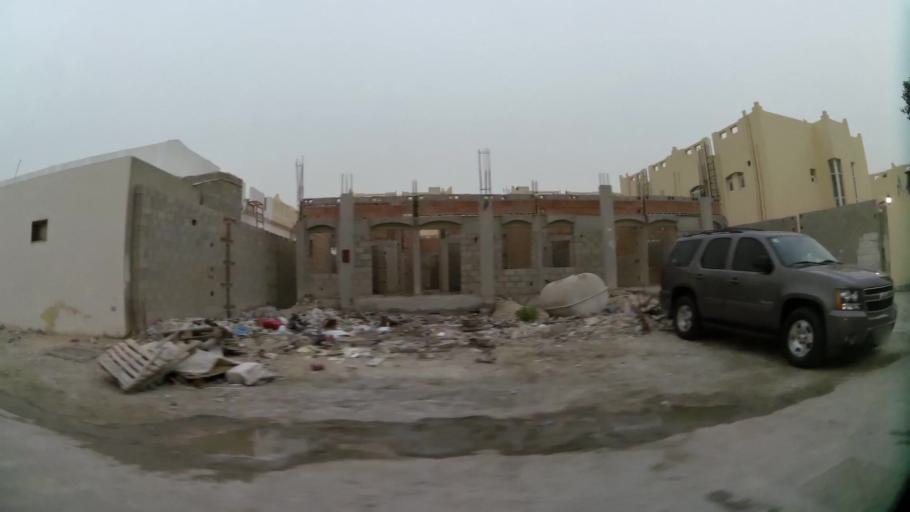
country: QA
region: Baladiyat ad Dawhah
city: Doha
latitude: 25.2285
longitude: 51.4899
